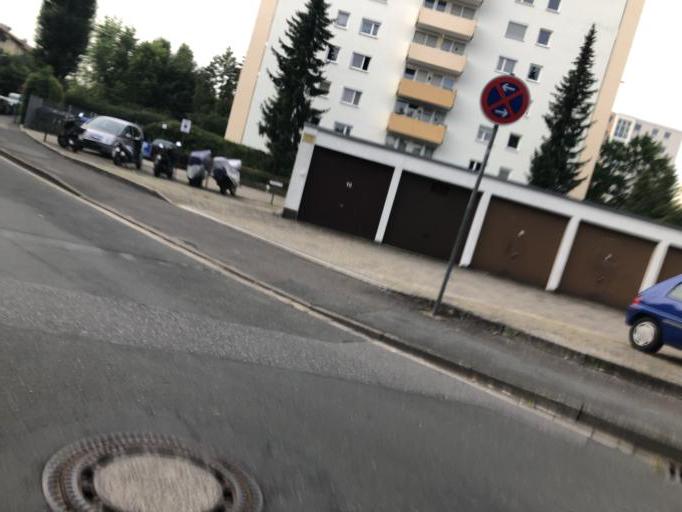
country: DE
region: Bavaria
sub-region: Regierungsbezirk Mittelfranken
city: Erlangen
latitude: 49.5784
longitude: 10.9953
